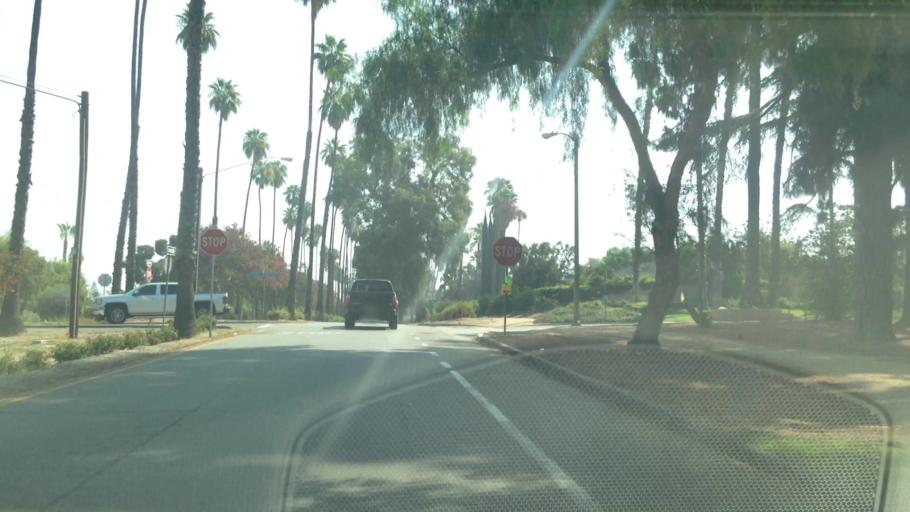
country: US
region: California
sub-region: Riverside County
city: Riverside
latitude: 33.9339
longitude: -117.3822
